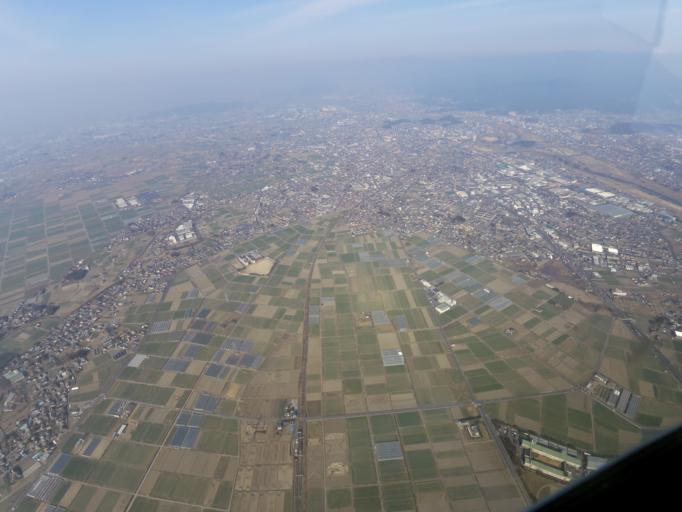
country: JP
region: Tochigi
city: Ashikaga
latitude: 36.2923
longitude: 139.4706
